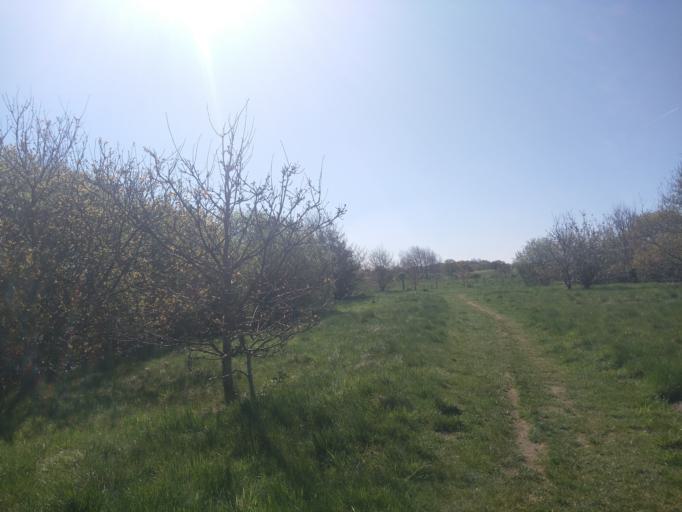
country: DK
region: Central Jutland
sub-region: Viborg Kommune
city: Viborg
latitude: 56.4411
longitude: 9.4321
